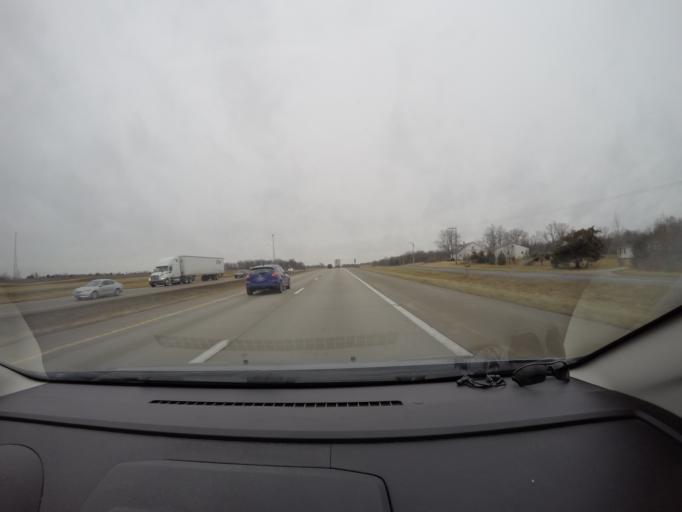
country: US
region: Missouri
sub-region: Montgomery County
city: Montgomery City
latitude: 38.9071
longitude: -91.6513
